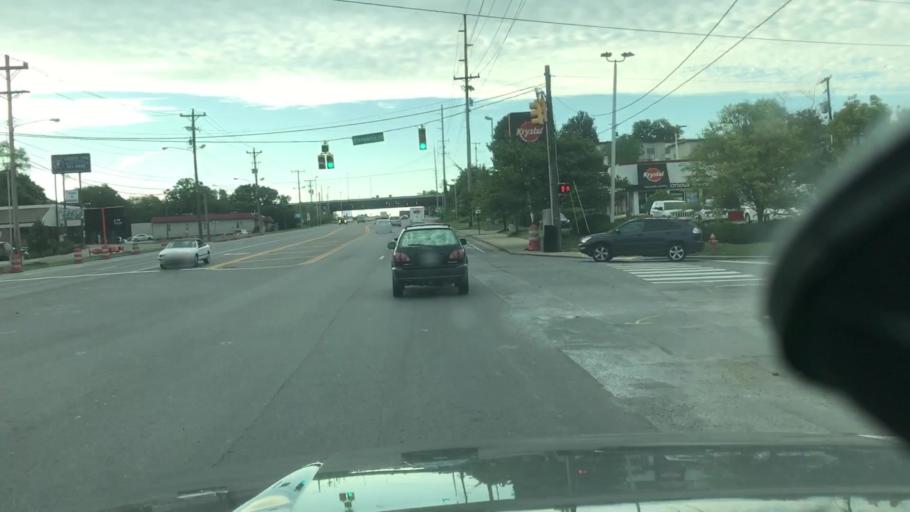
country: US
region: Tennessee
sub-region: Davidson County
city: Oak Hill
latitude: 36.1208
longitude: -86.7037
